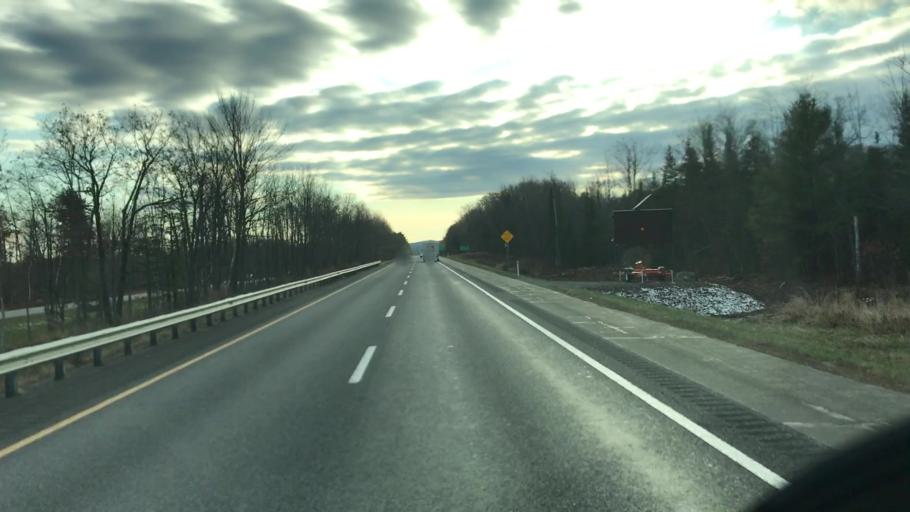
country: US
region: Maine
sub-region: Kennebec County
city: Oakland
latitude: 44.5374
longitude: -69.6858
